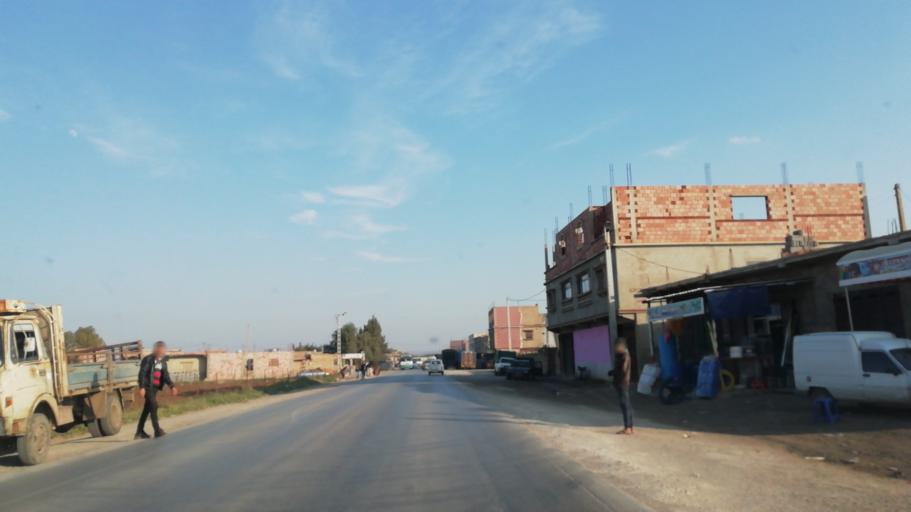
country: DZ
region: Relizane
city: Djidiouia
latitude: 35.8967
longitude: 0.6918
